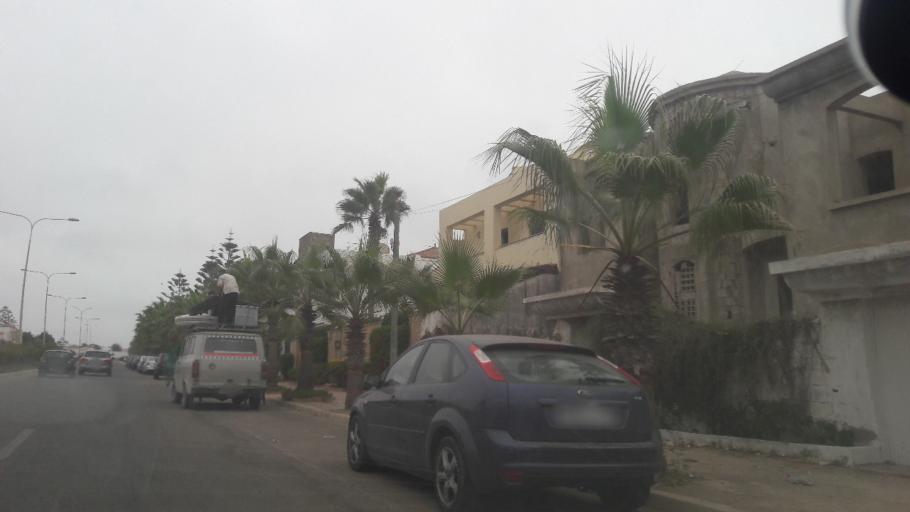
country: MA
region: Souss-Massa-Draa
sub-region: Agadir-Ida-ou-Tnan
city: Agadir
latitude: 30.3921
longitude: -9.5950
